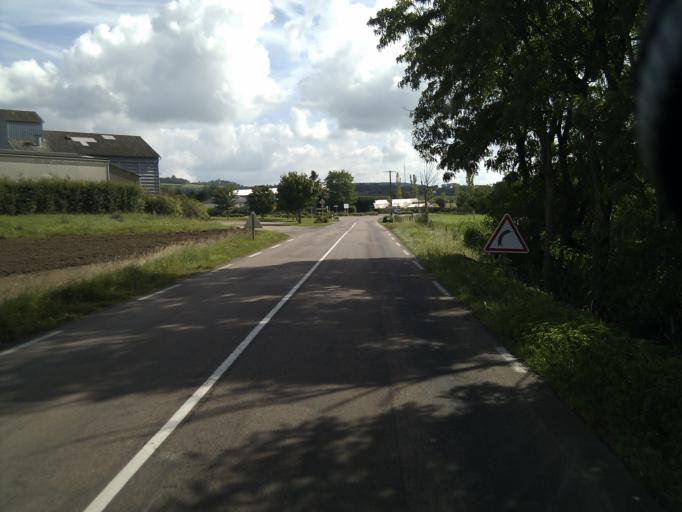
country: FR
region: Bourgogne
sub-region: Departement de la Cote-d'Or
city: Semur-en-Auxois
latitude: 47.3970
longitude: 4.3045
